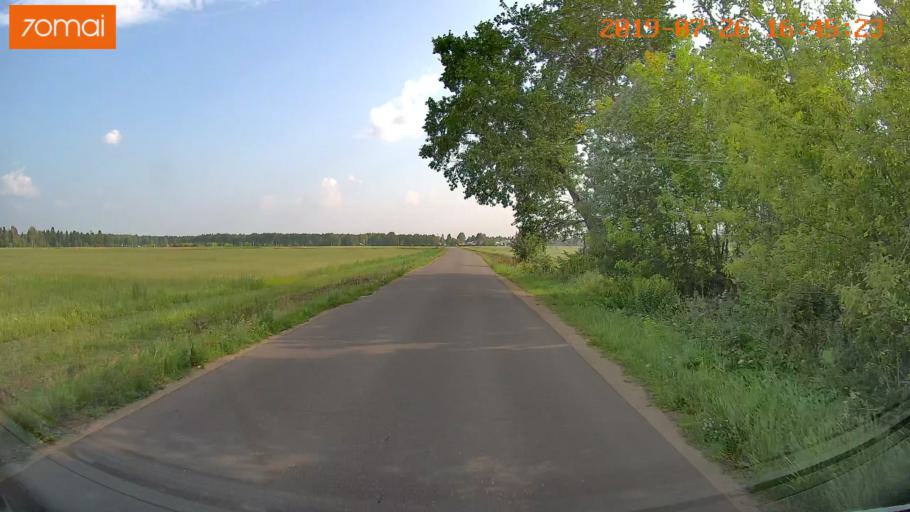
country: RU
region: Ivanovo
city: Bogorodskoye
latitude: 57.0508
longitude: 41.0220
